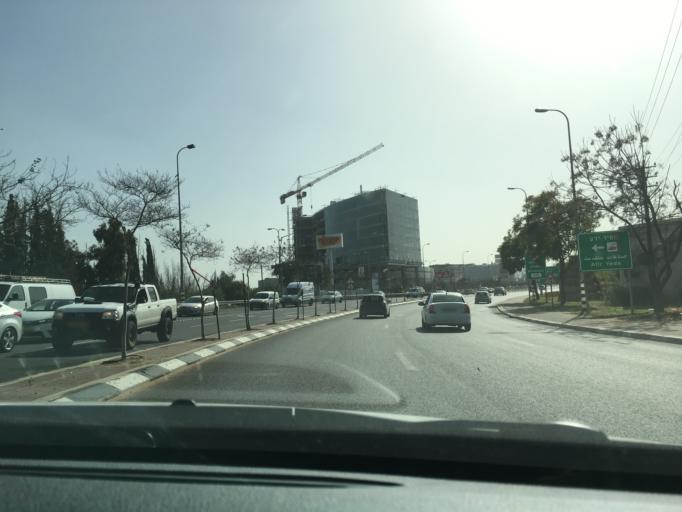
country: IL
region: Central District
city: Kfar Saba
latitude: 32.1699
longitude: 34.9287
